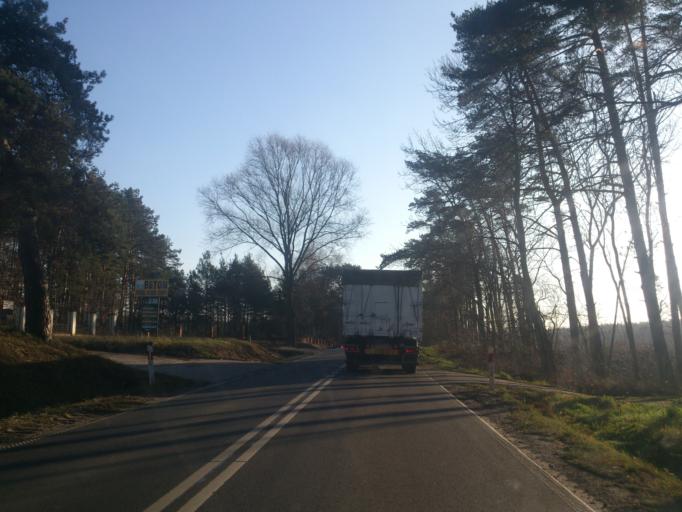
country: PL
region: Kujawsko-Pomorskie
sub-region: Powiat golubsko-dobrzynski
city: Golub-Dobrzyn
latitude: 53.1058
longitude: 19.1232
